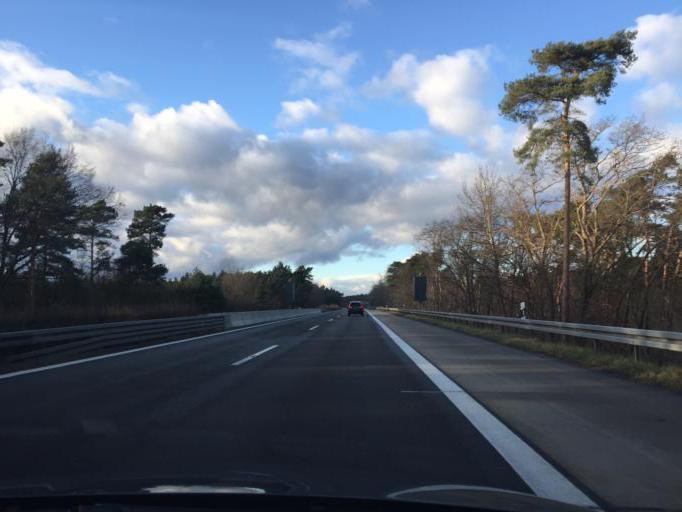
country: DE
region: Brandenburg
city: Vetschau
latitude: 51.8194
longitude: 14.0150
